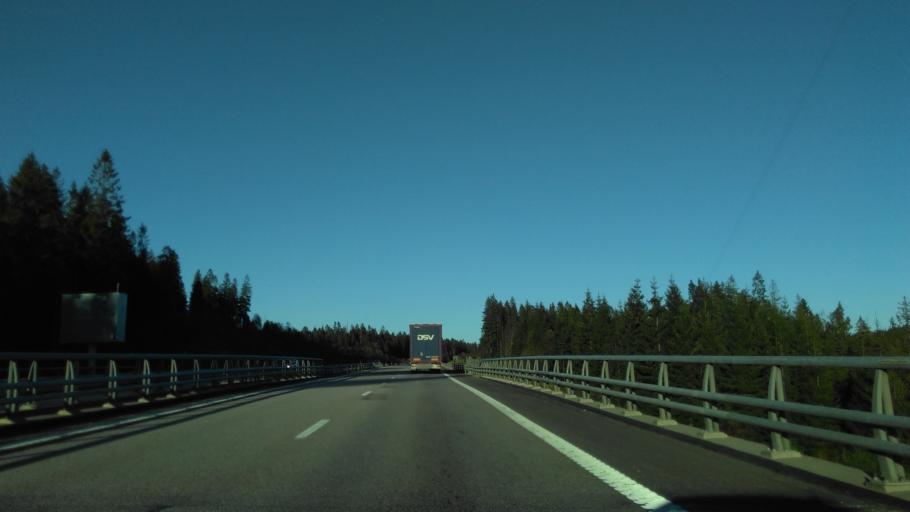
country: SE
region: Vaestra Goetaland
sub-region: Boras Kommun
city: Ganghester
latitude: 57.7346
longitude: 13.0385
